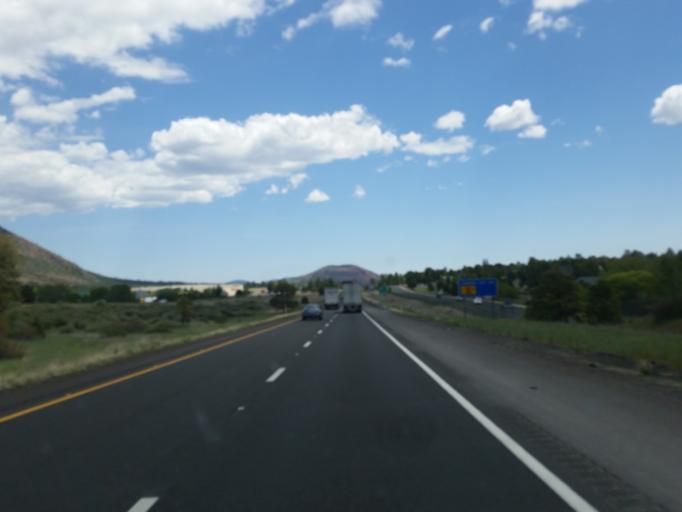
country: US
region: Arizona
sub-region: Coconino County
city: Flagstaff
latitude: 35.2028
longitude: -111.6065
